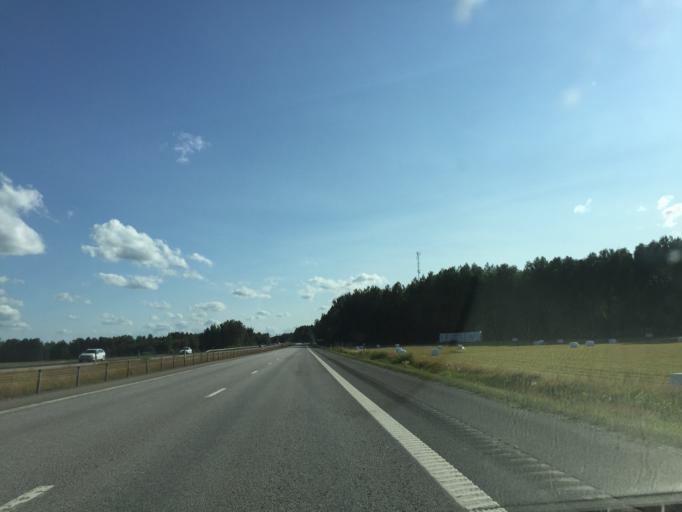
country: SE
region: OErebro
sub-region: Kumla Kommun
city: Kumla
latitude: 59.1453
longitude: 15.0912
